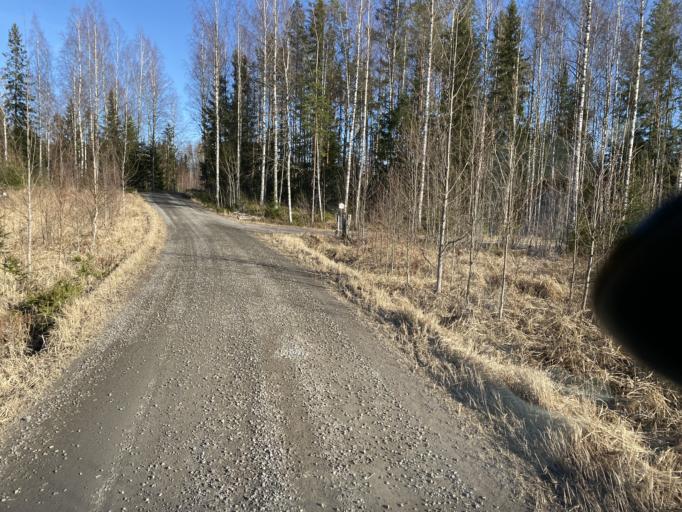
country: FI
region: Satakunta
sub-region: Rauma
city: Lappi
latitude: 61.1476
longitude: 21.8944
